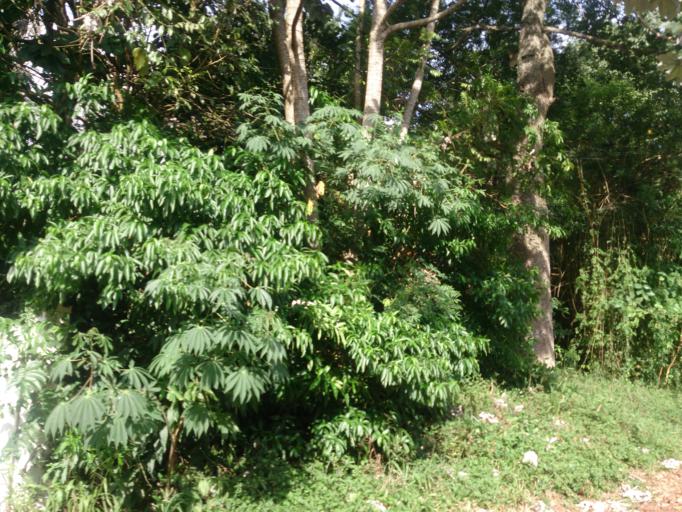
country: AR
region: Misiones
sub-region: Departamento de Obera
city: Obera
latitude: -27.4985
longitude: -55.1121
